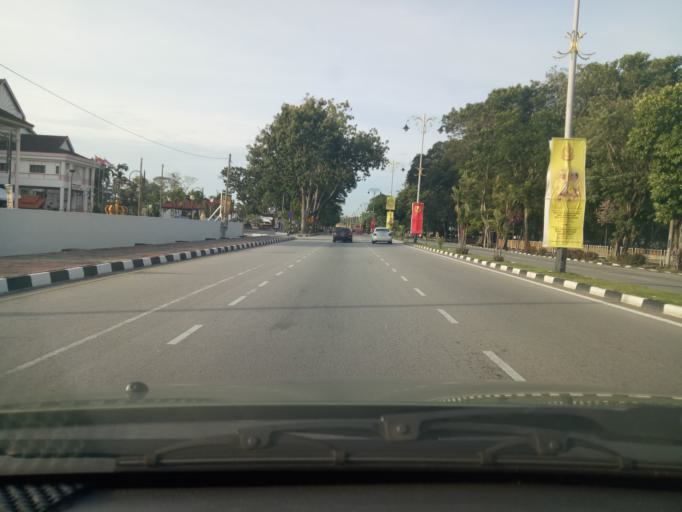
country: MY
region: Kedah
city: Alor Setar
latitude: 6.1352
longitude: 100.3693
